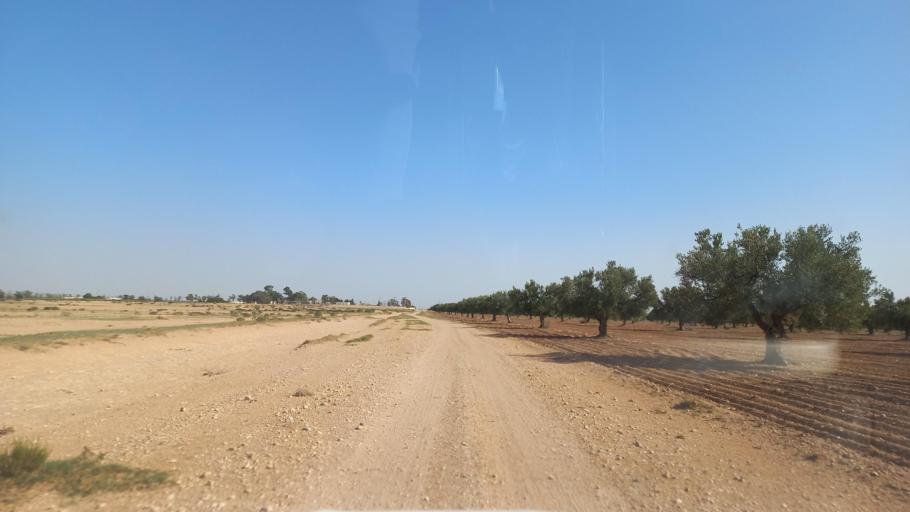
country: TN
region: Al Qasrayn
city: Kasserine
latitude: 35.3011
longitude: 9.0269
